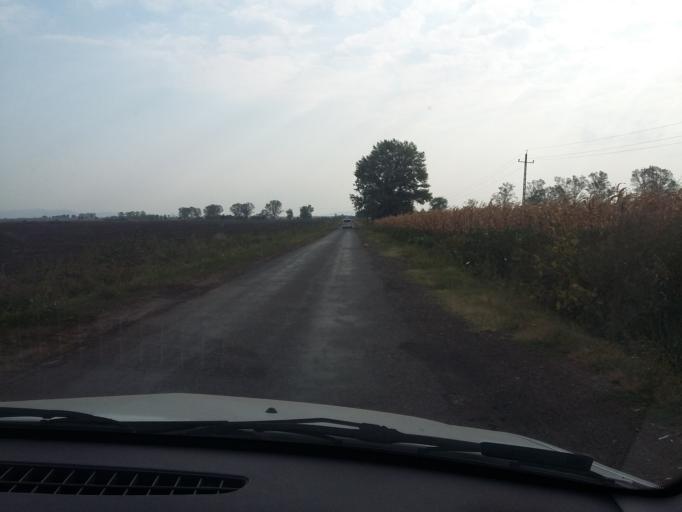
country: HU
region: Borsod-Abauj-Zemplen
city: Taktaharkany
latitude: 48.1204
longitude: 21.1085
